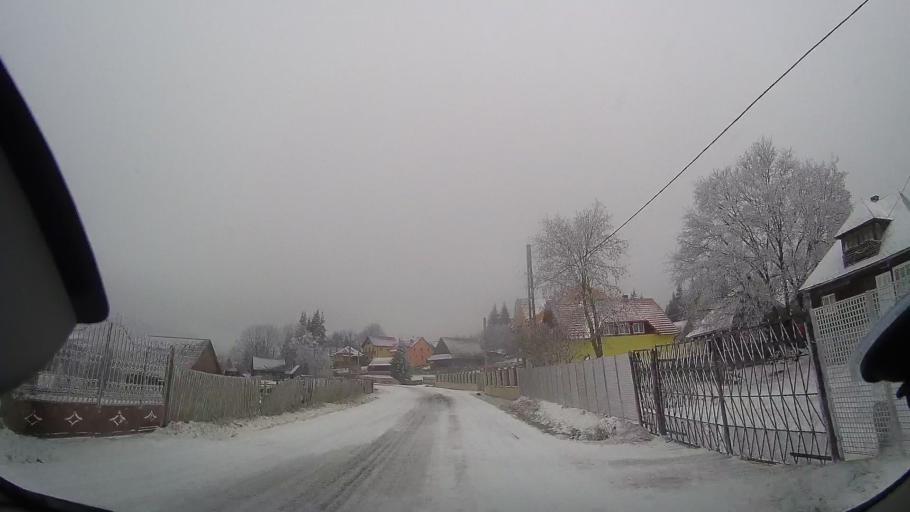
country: RO
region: Cluj
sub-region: Comuna Maguri-Racatau
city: Maguri
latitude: 46.6499
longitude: 23.0785
